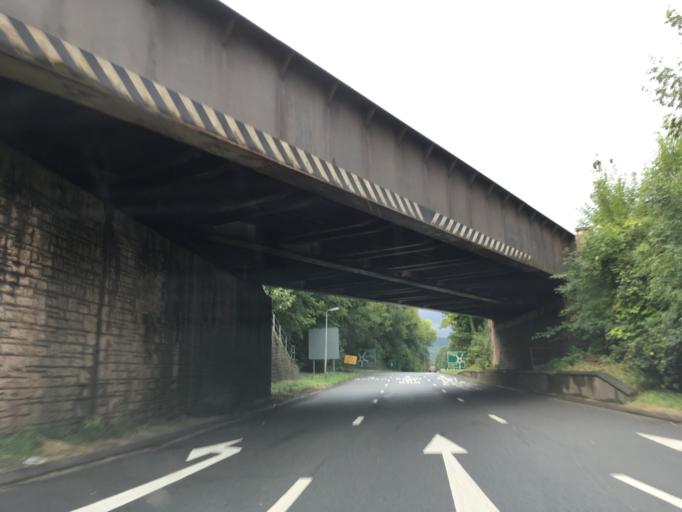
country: GB
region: Wales
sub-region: Monmouthshire
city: Abergavenny
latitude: 51.8080
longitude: -3.0073
